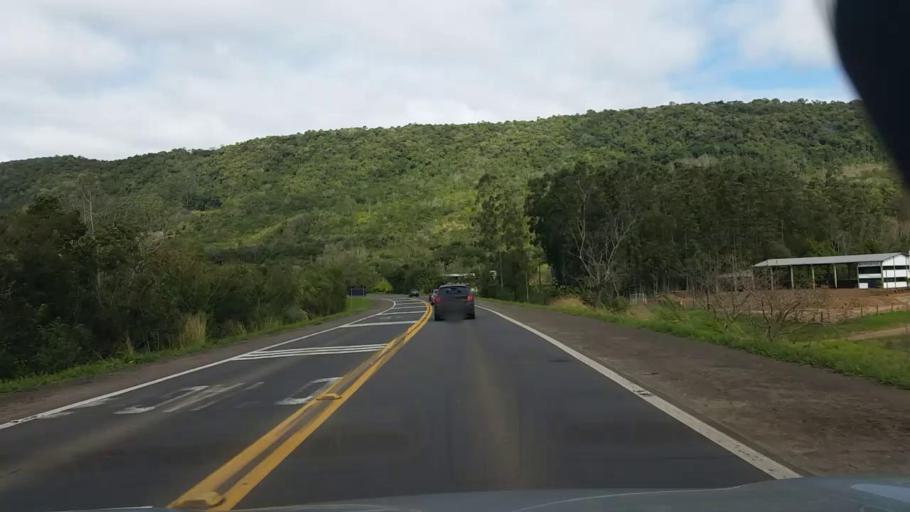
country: BR
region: Rio Grande do Sul
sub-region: Arroio Do Meio
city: Arroio do Meio
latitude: -29.3286
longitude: -52.1017
